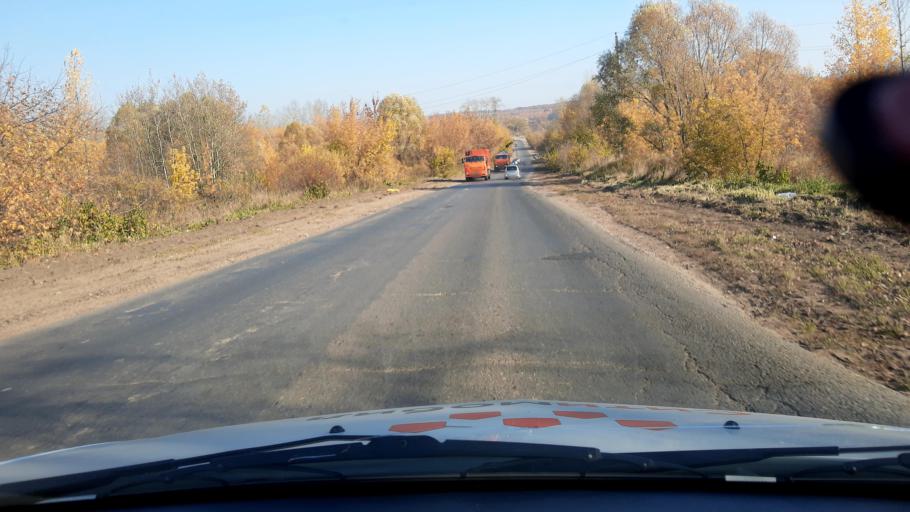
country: RU
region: Bashkortostan
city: Ufa
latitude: 54.8631
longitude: 56.1200
